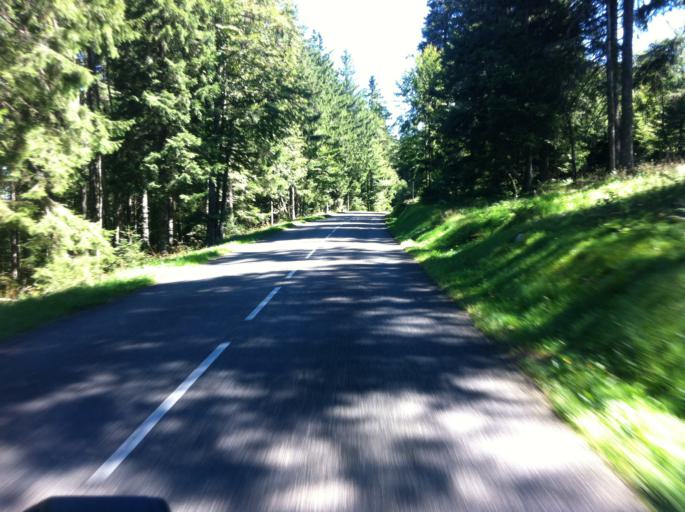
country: FR
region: Lorraine
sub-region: Departement des Vosges
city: Plainfaing
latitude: 48.1308
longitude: 7.0742
